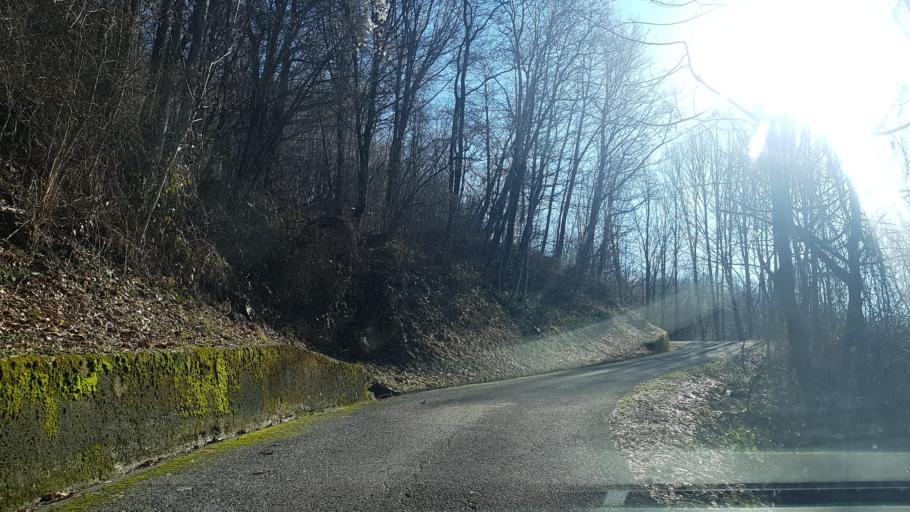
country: IT
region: Friuli Venezia Giulia
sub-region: Provincia di Udine
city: Isola
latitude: 46.2632
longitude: 13.2233
